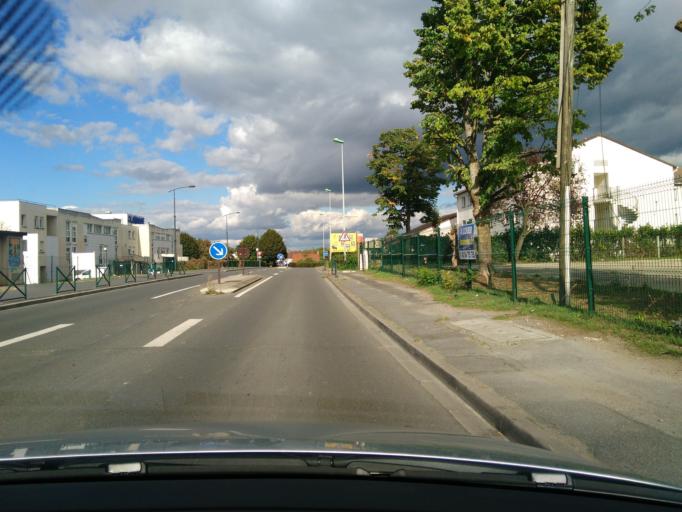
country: FR
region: Ile-de-France
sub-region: Departement de Seine-et-Marne
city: Villenoy
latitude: 48.9399
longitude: 2.8728
